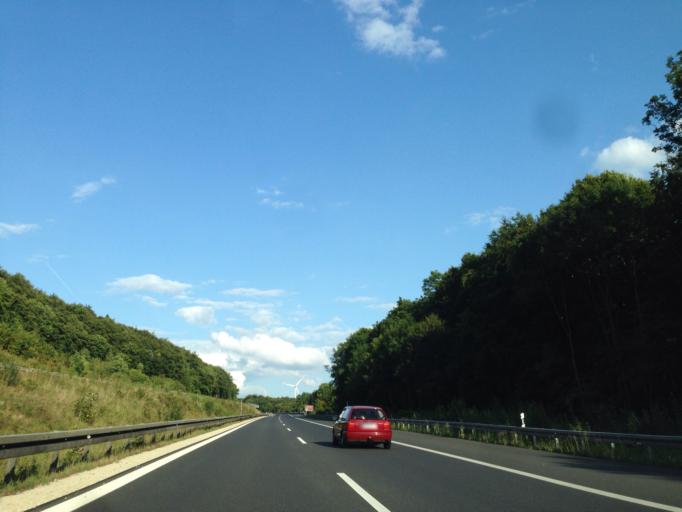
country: DE
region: Bavaria
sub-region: Upper Franconia
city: Schesslitz
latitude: 49.9841
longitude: 11.0806
